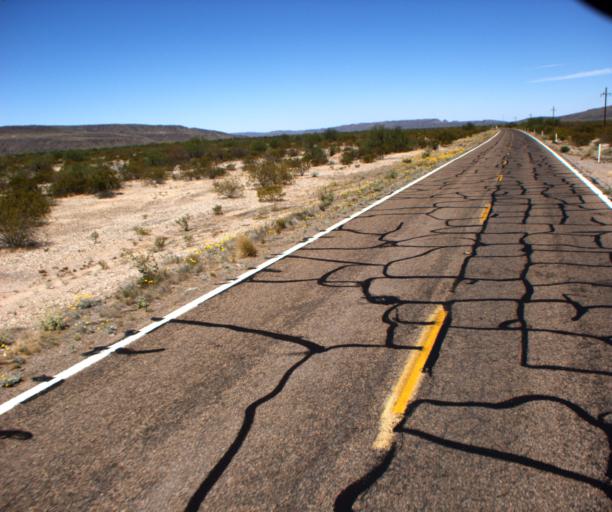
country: US
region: Arizona
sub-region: Pima County
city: Ajo
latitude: 32.4482
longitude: -112.8711
